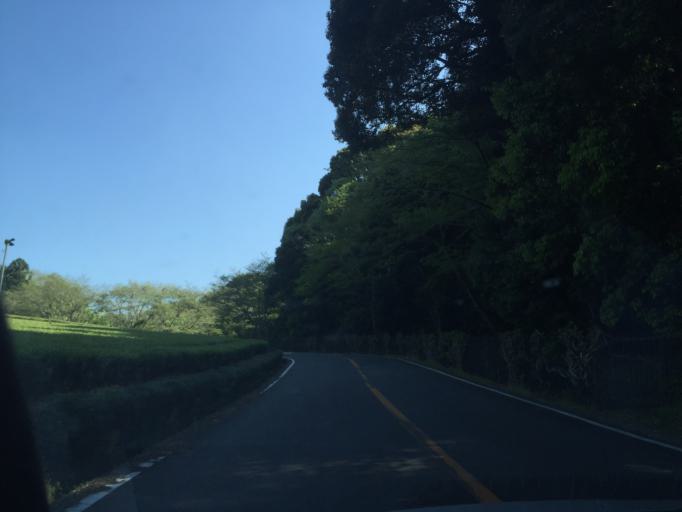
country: JP
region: Shizuoka
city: Kakegawa
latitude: 34.7703
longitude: 138.0524
